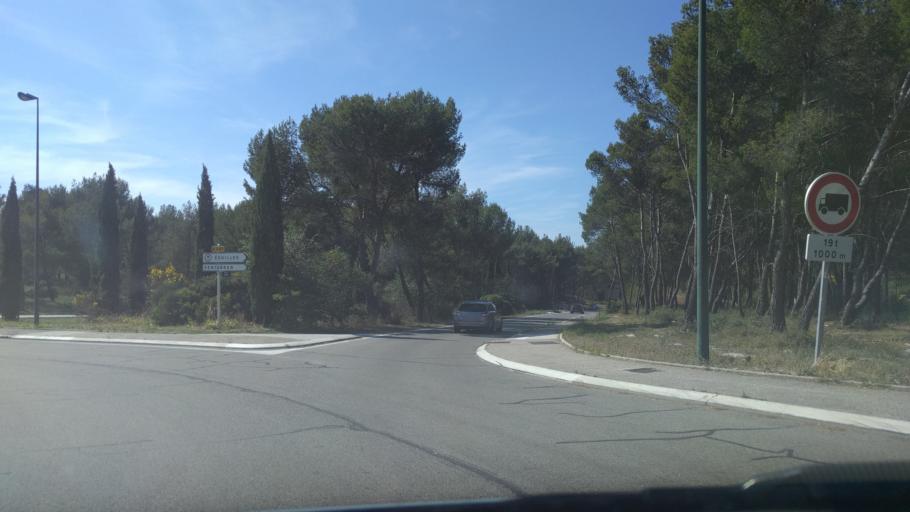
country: FR
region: Provence-Alpes-Cote d'Azur
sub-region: Departement des Bouches-du-Rhone
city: Cabries
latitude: 43.4957
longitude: 5.3505
